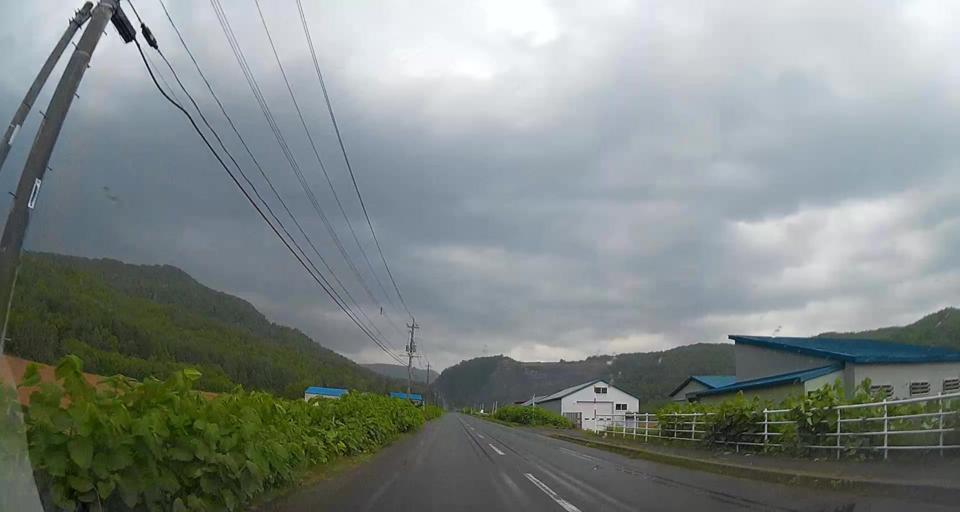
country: JP
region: Hokkaido
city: Niseko Town
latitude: 42.8909
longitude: 140.8961
